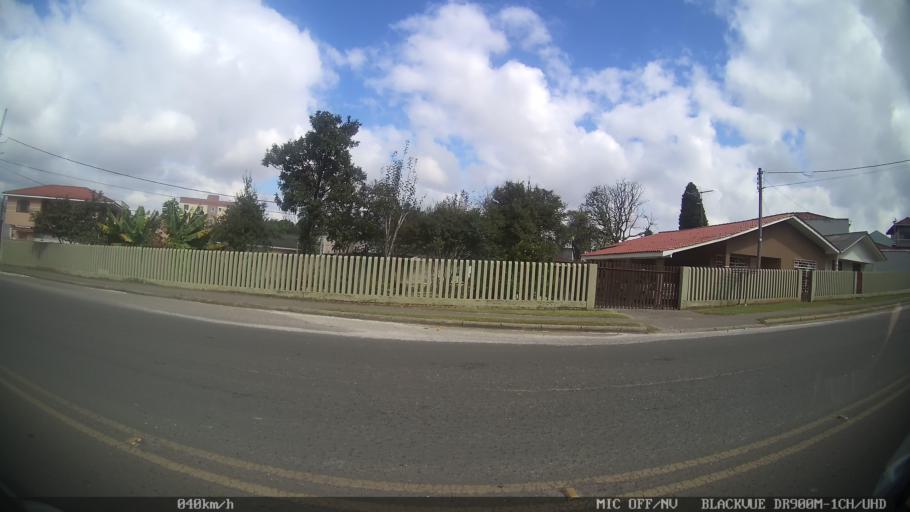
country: BR
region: Parana
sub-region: Colombo
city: Colombo
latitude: -25.3480
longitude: -49.1794
